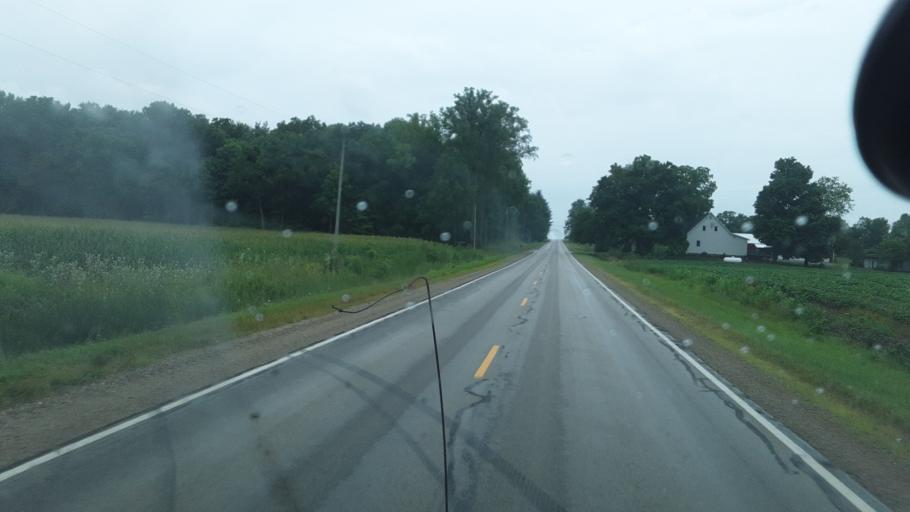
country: US
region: Indiana
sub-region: Steuben County
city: Hamilton
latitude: 41.5587
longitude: -84.8459
